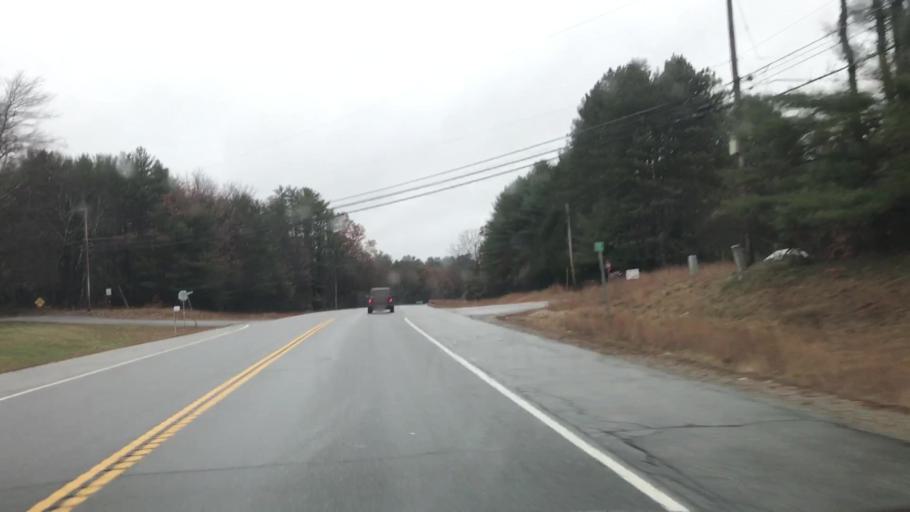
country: US
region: New Hampshire
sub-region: Merrimack County
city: Pittsfield
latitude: 43.2852
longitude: -71.3606
